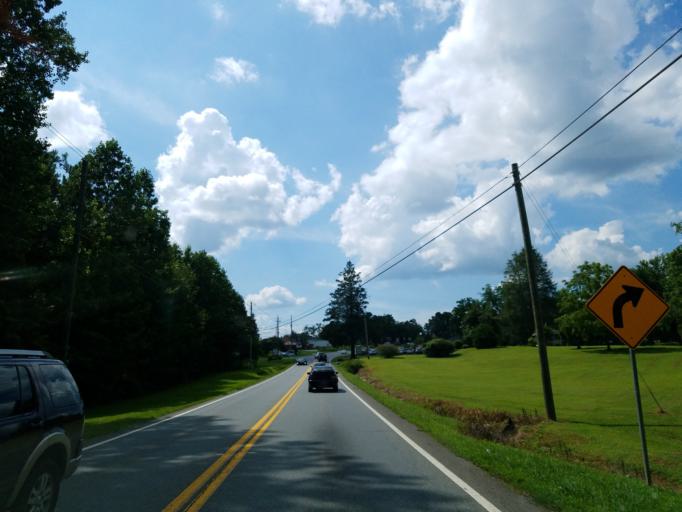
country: US
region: Georgia
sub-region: Dawson County
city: Dawsonville
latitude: 34.4143
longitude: -84.1109
